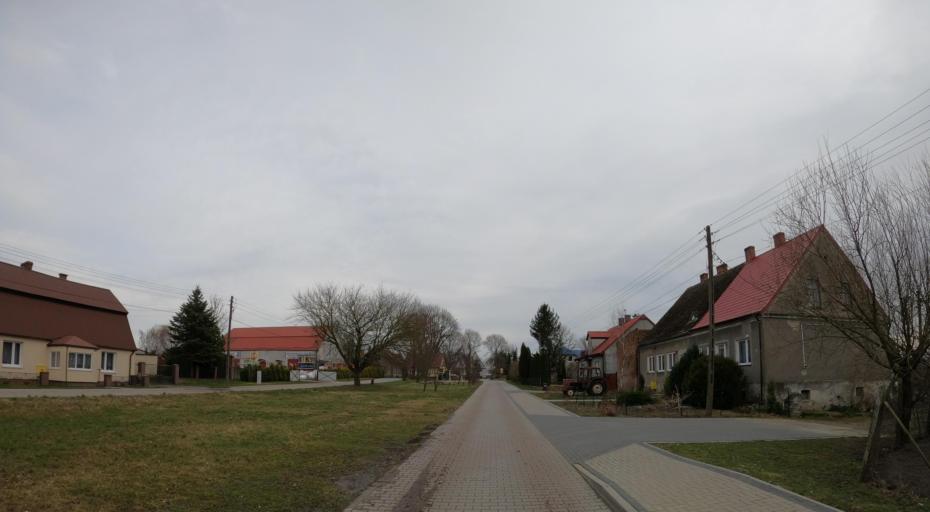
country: PL
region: West Pomeranian Voivodeship
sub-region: Powiat pyrzycki
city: Pyrzyce
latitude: 53.1601
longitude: 14.8400
